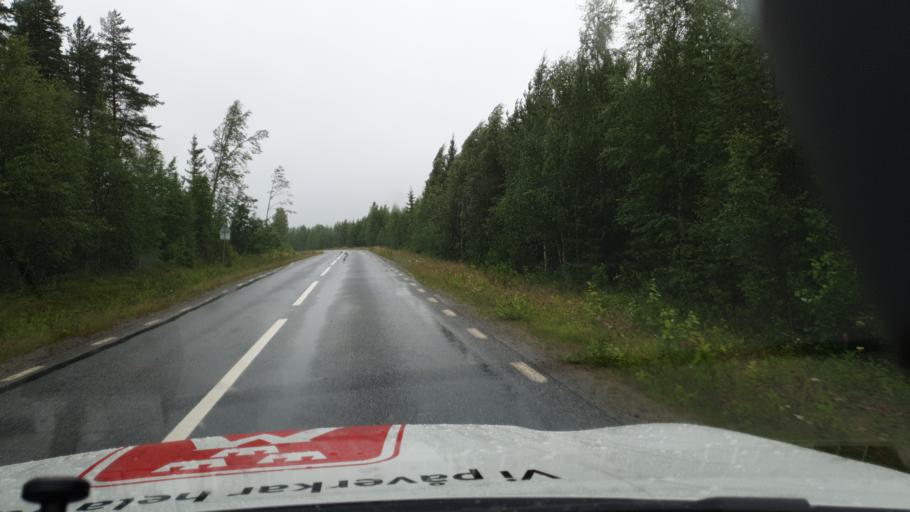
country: SE
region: Vaesterbotten
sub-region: Skelleftea Kommun
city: Burtraesk
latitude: 64.5049
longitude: 20.4632
